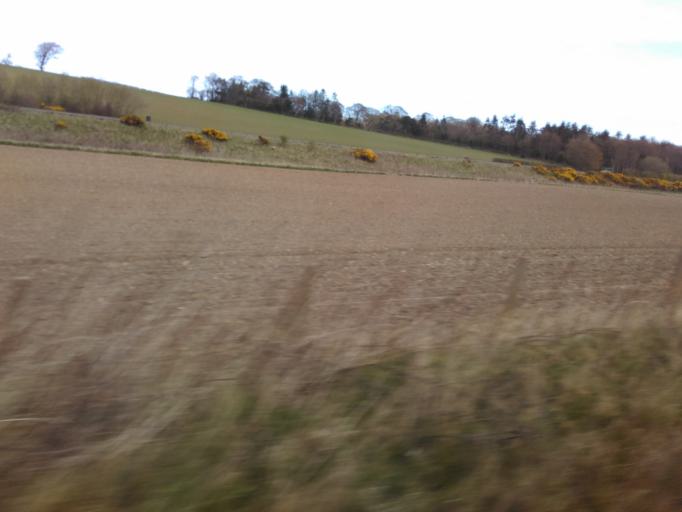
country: GB
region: Scotland
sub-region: The Scottish Borders
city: Chirnside
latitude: 55.8583
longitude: -2.2415
